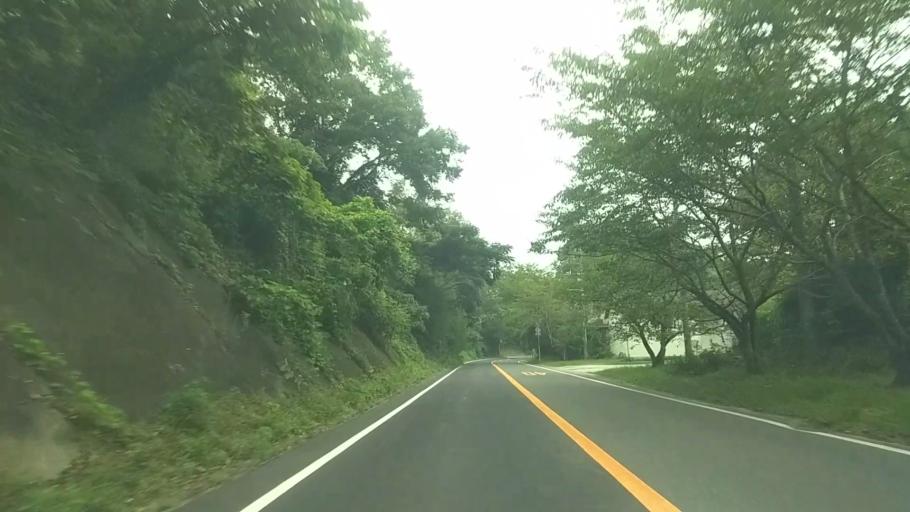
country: JP
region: Chiba
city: Kimitsu
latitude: 35.2220
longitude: 139.9503
